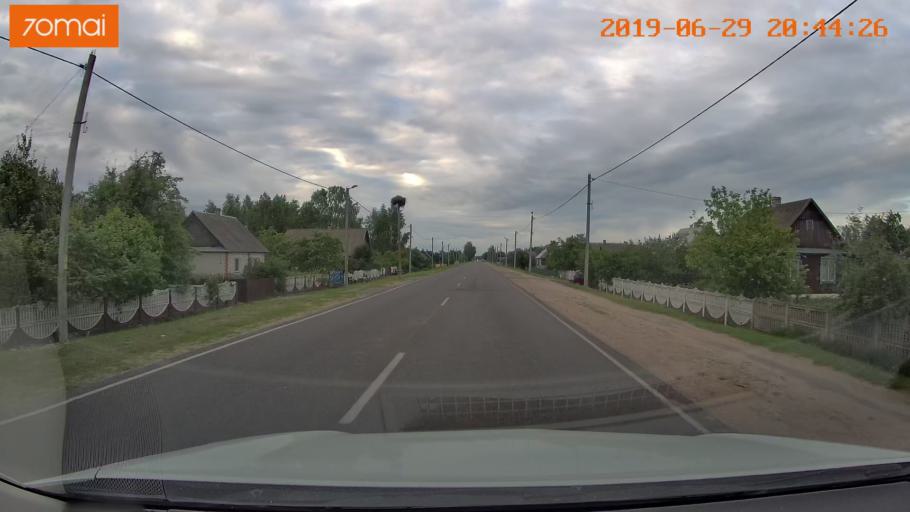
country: BY
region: Brest
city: Hantsavichy
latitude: 52.6136
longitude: 26.3073
